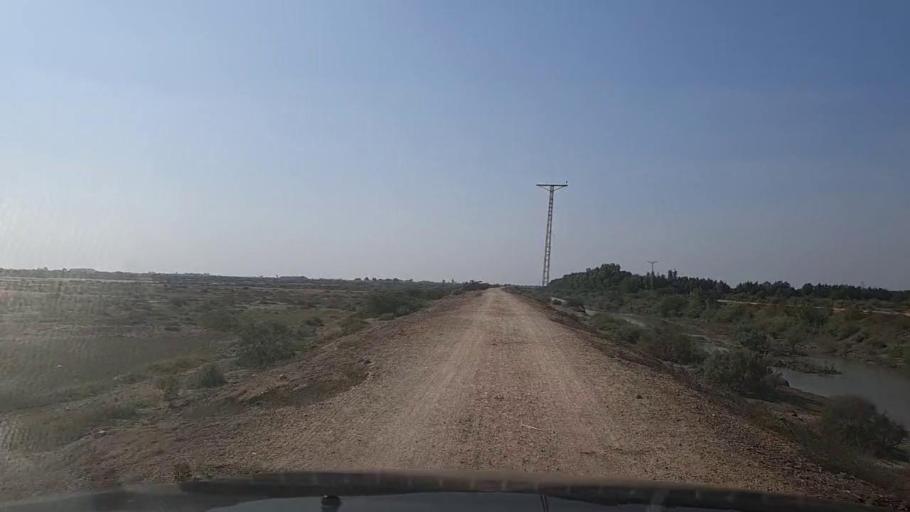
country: PK
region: Sindh
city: Thatta
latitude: 24.7111
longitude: 67.7647
